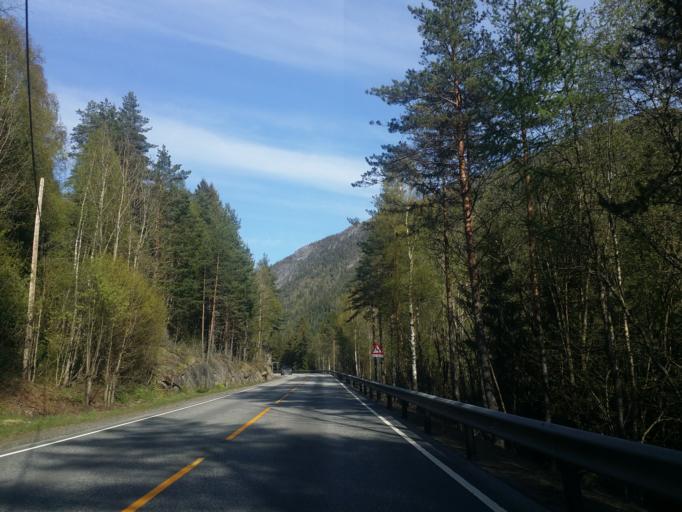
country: NO
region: Telemark
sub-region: Hjartdal
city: Sauland
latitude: 59.6101
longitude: 8.7782
